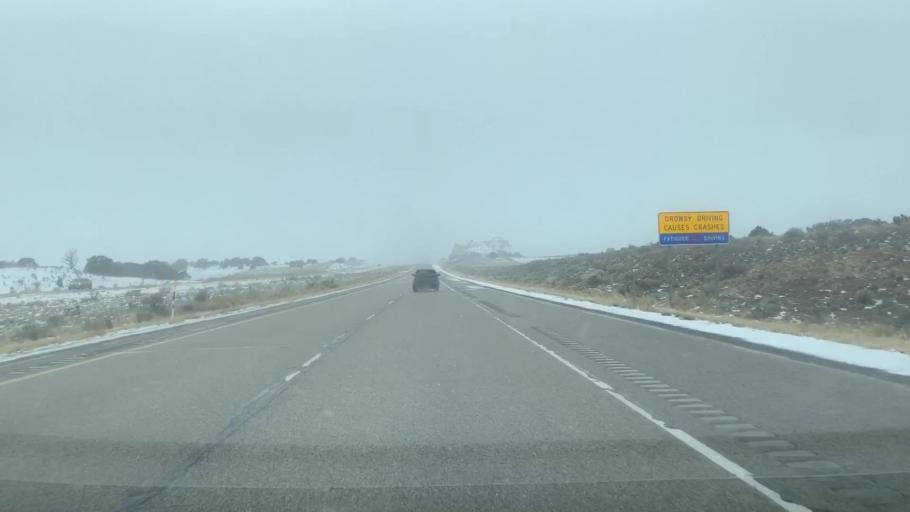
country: US
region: Utah
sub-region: Emery County
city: Castle Dale
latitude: 38.8723
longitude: -110.7650
